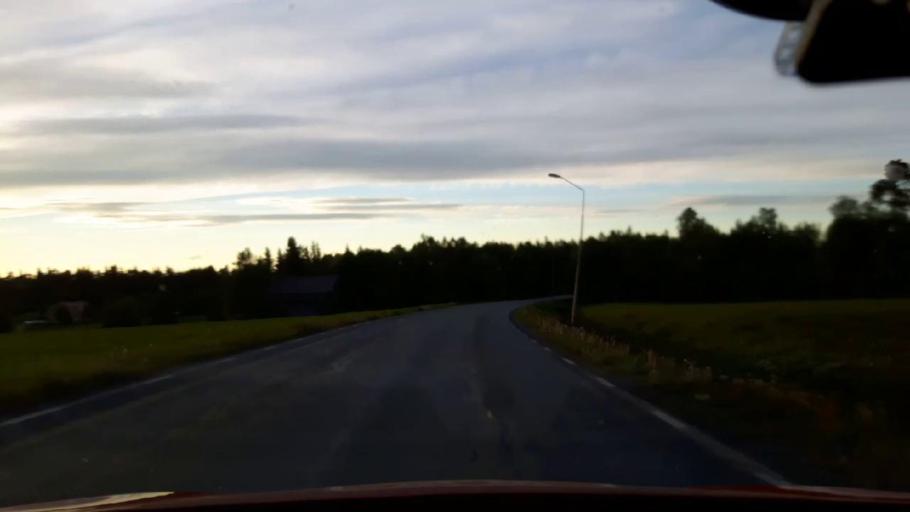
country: SE
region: Jaemtland
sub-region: Krokoms Kommun
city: Krokom
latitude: 63.1191
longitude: 14.4318
